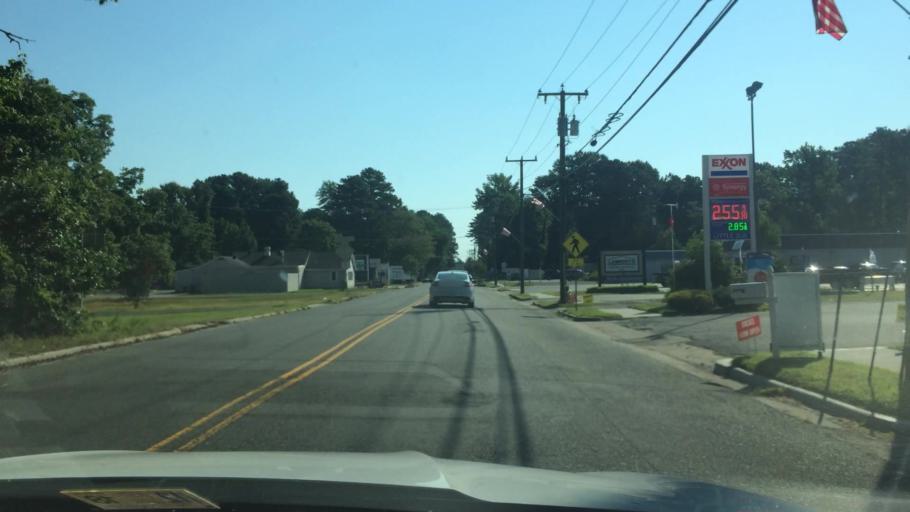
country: US
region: Virginia
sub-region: Lancaster County
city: Kilmarnock
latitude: 37.6455
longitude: -76.3954
